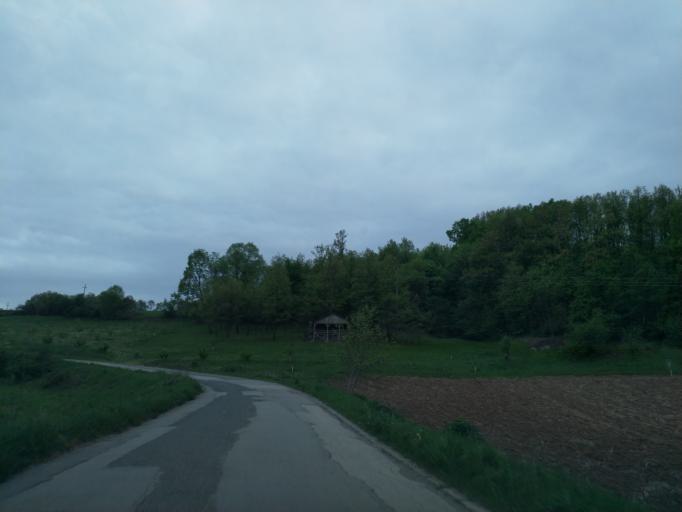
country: RS
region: Central Serbia
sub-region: Pomoravski Okrug
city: Cuprija
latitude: 43.9534
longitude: 21.4837
